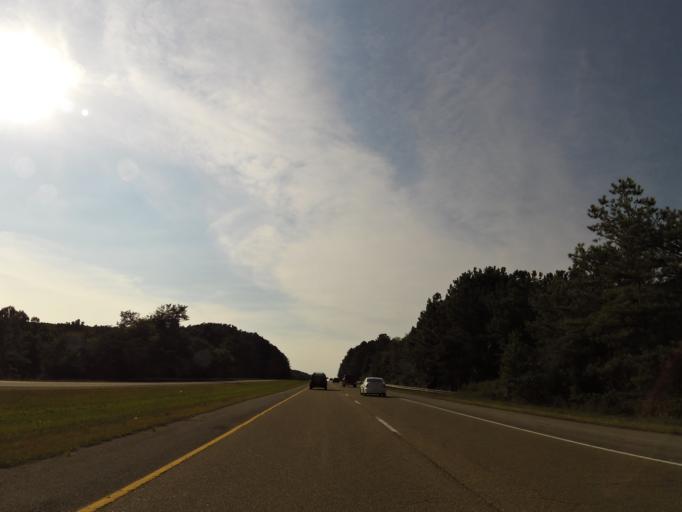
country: US
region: Tennessee
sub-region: Loudon County
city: Lenoir City
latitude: 35.8434
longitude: -84.3147
